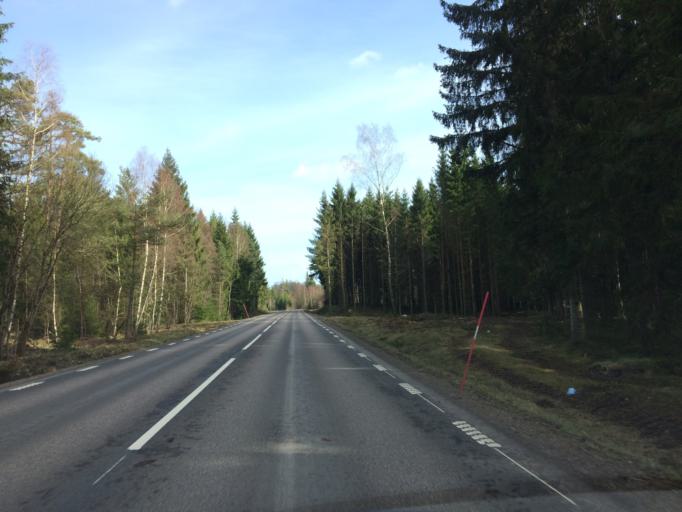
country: SE
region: Halland
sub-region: Hylte Kommun
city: Torup
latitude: 57.0242
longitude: 13.1201
